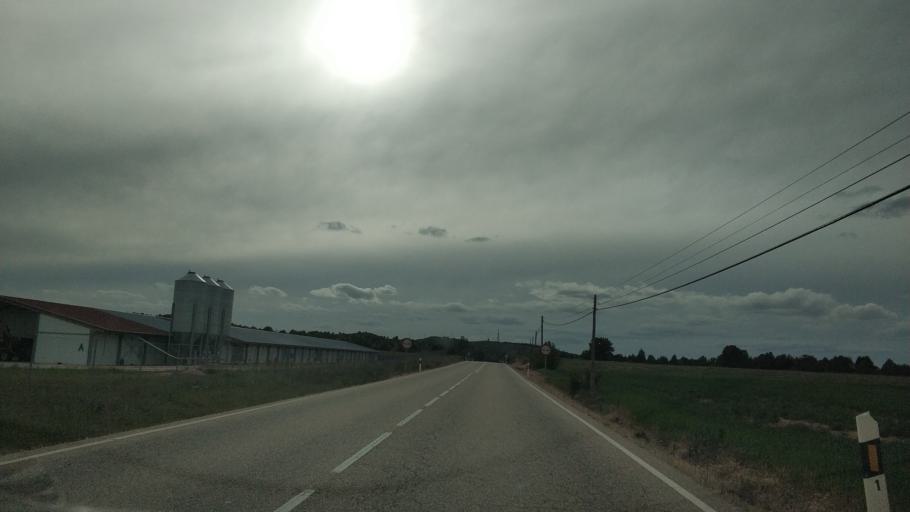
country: ES
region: Castille and Leon
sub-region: Provincia de Soria
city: El Burgo de Osma
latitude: 41.5751
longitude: -3.0232
